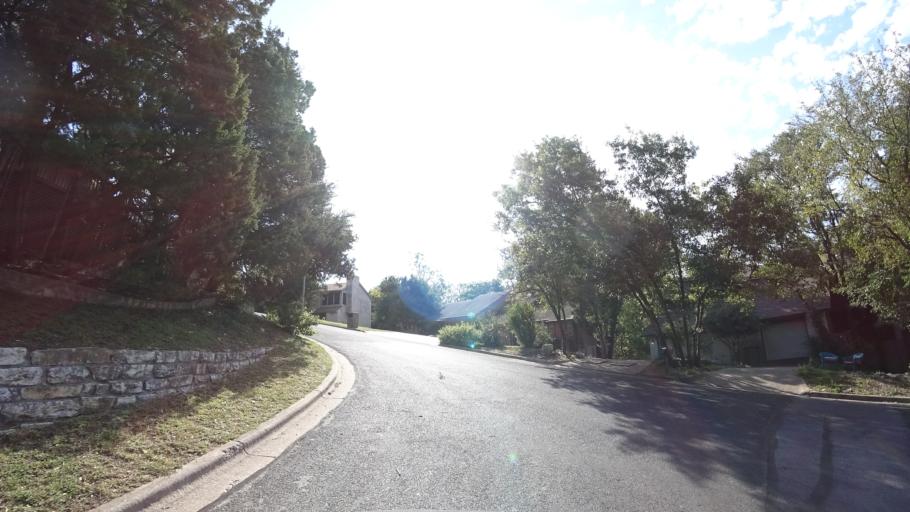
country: US
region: Texas
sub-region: Travis County
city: West Lake Hills
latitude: 30.3462
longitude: -97.7565
